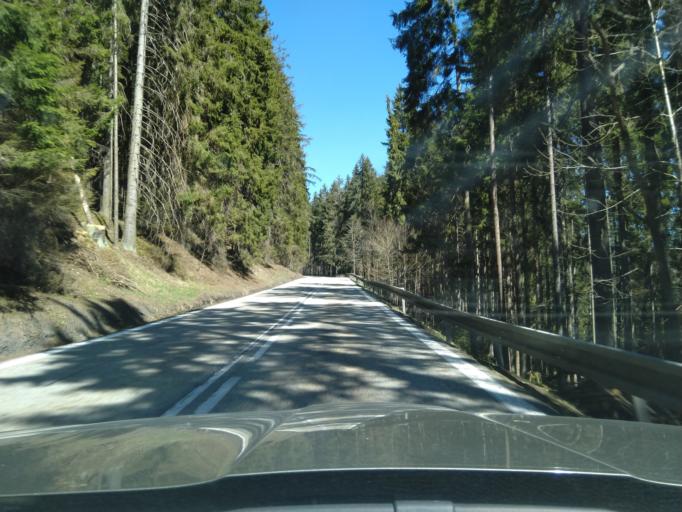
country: CZ
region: Jihocesky
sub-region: Okres Prachatice
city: Vimperk
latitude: 48.9695
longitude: 13.7609
